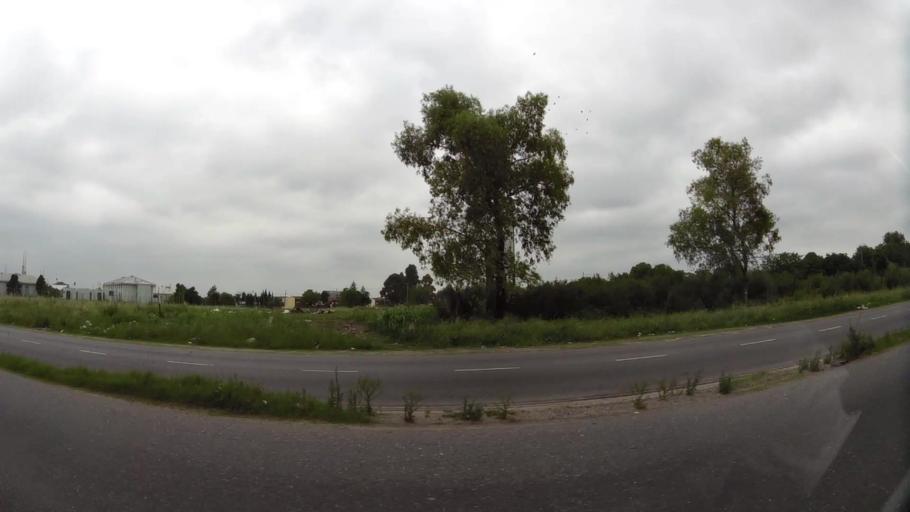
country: AR
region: Buenos Aires
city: San Justo
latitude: -34.7273
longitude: -58.5211
